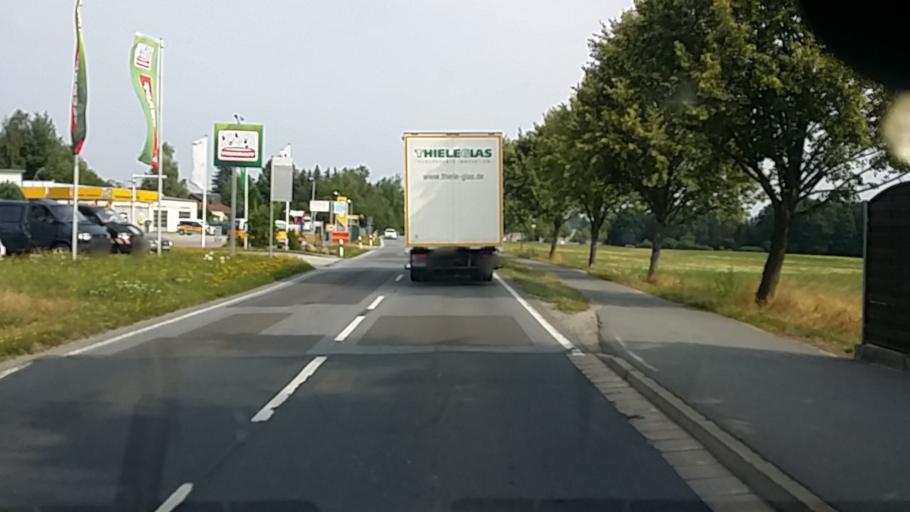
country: DE
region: Saxony
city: Radeberg
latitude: 51.1318
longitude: 13.9172
